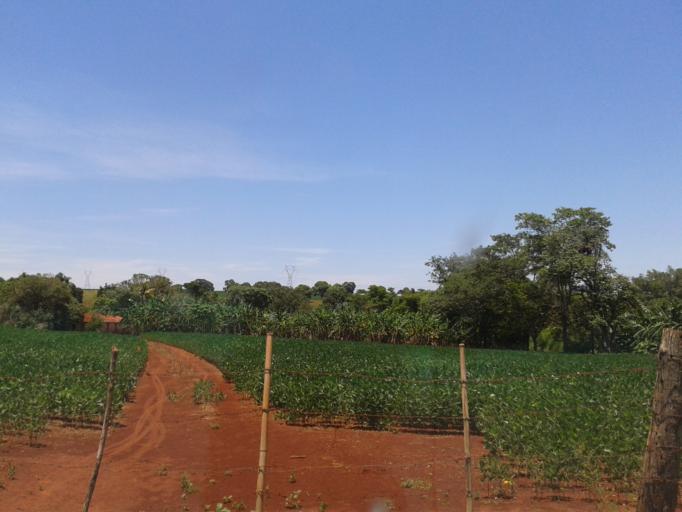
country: BR
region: Minas Gerais
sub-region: Centralina
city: Centralina
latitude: -18.6197
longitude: -49.2956
